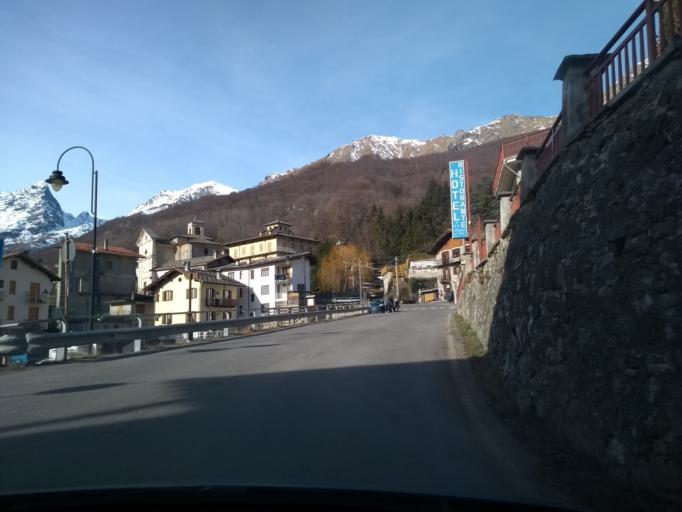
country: IT
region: Piedmont
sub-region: Provincia di Torino
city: Ala di Stura
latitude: 45.3150
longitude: 7.3066
